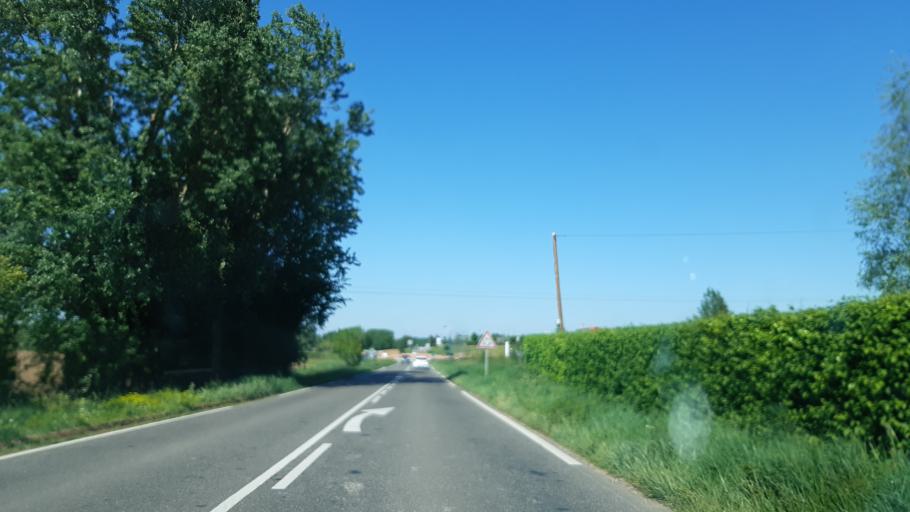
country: FR
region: Midi-Pyrenees
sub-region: Departement du Gers
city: Pujaudran
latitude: 43.5995
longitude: 1.0661
